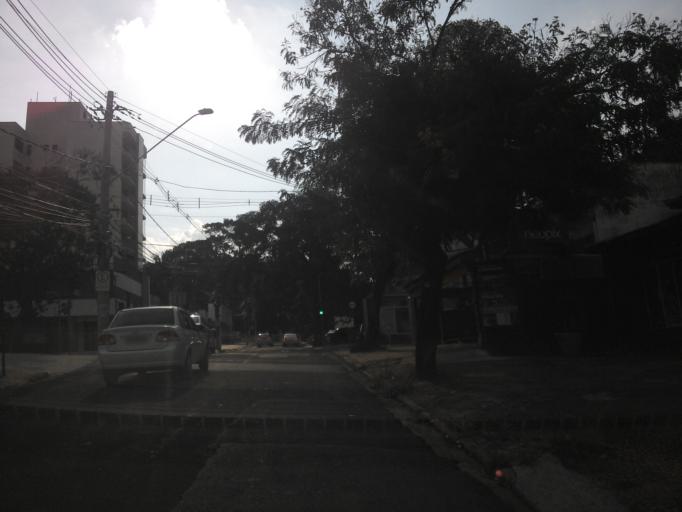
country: BR
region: Sao Paulo
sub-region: Campinas
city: Campinas
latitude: -22.8938
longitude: -47.0634
